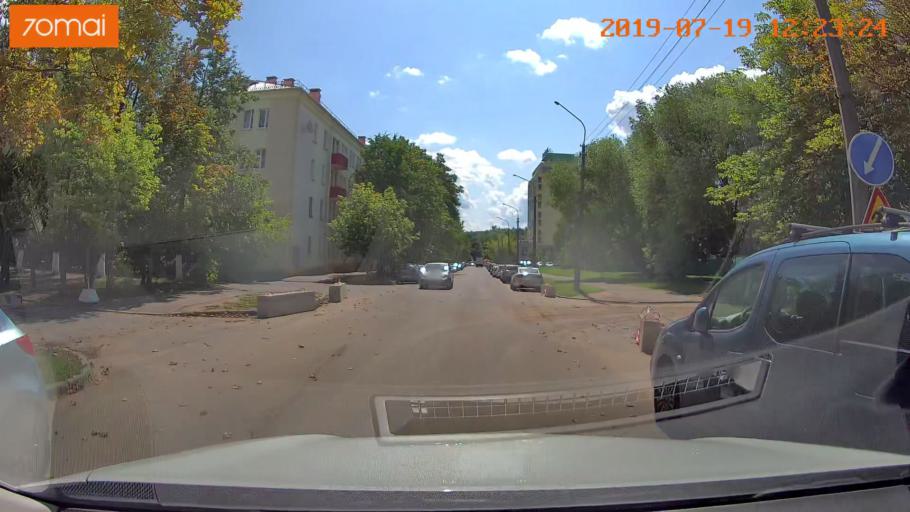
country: BY
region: Minsk
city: Minsk
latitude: 53.9280
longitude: 27.6180
